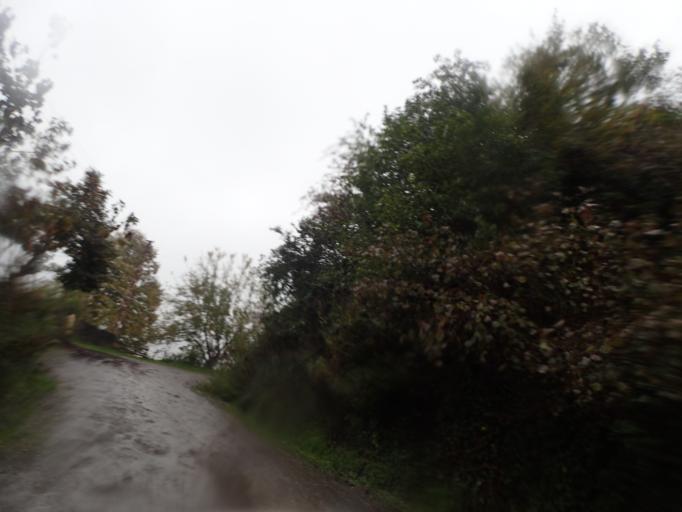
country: TR
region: Ordu
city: Persembe
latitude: 41.0286
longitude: 37.7210
